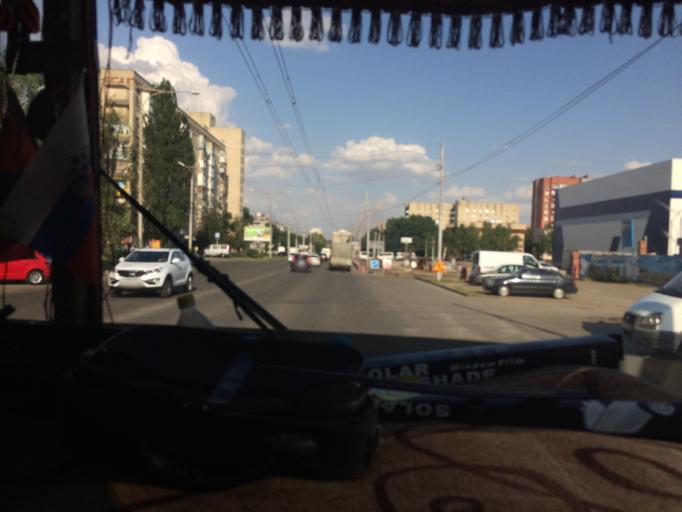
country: RU
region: Stavropol'skiy
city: Stavropol'
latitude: 45.0134
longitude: 41.9210
